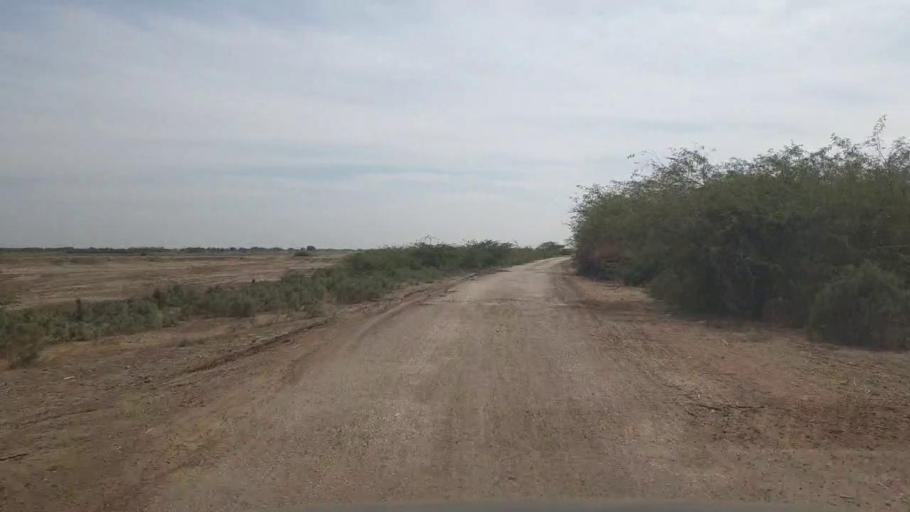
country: PK
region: Sindh
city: Kunri
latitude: 25.2686
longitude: 69.6019
